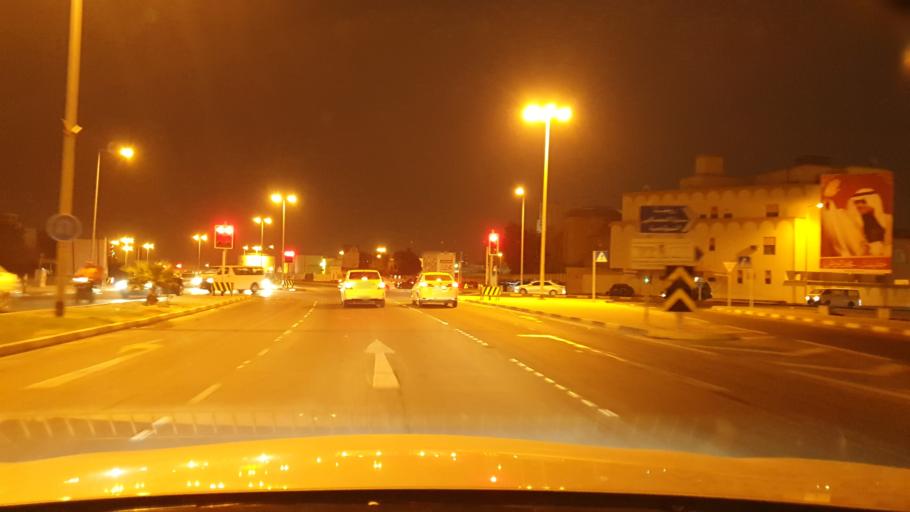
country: BH
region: Muharraq
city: Al Hadd
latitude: 26.2584
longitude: 50.6387
